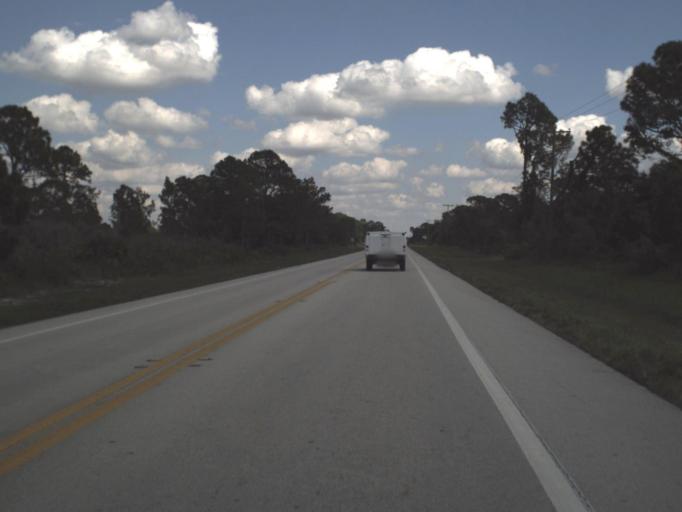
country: US
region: Florida
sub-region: Highlands County
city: Sebring
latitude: 27.4167
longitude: -81.4437
